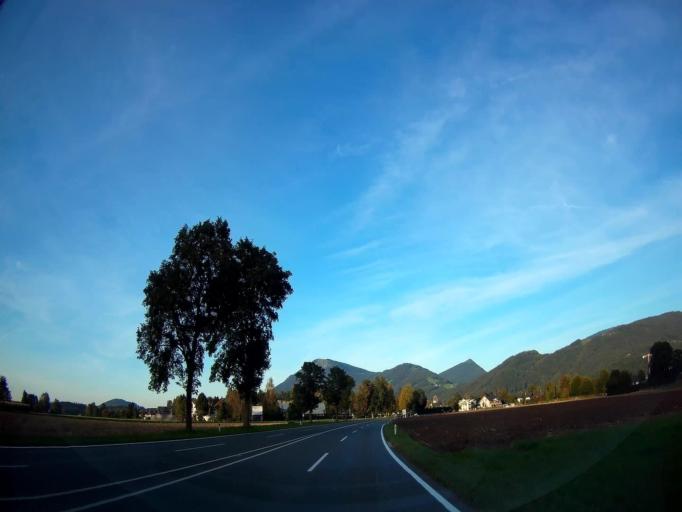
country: AT
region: Salzburg
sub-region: Politischer Bezirk Salzburg-Umgebung
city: Anif
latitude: 47.7427
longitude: 13.0593
